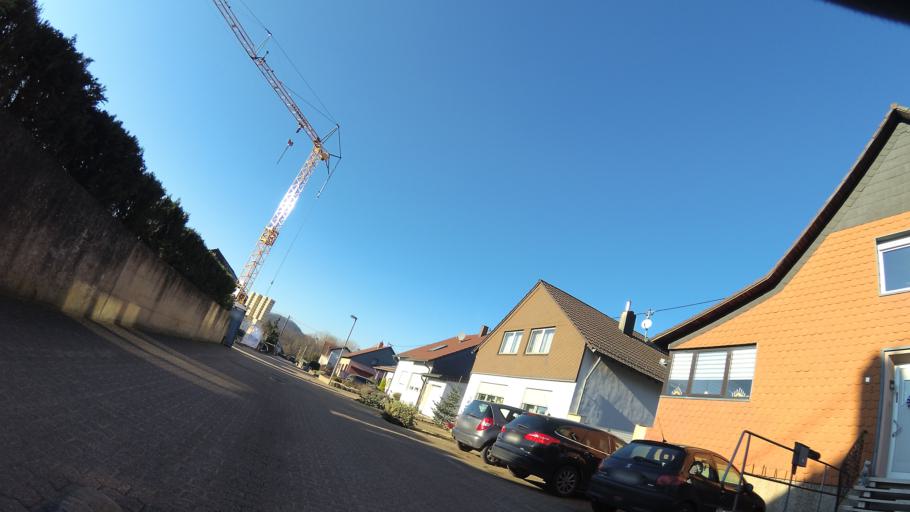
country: DE
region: Saarland
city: Wallerfangen
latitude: 49.3126
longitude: 6.7176
